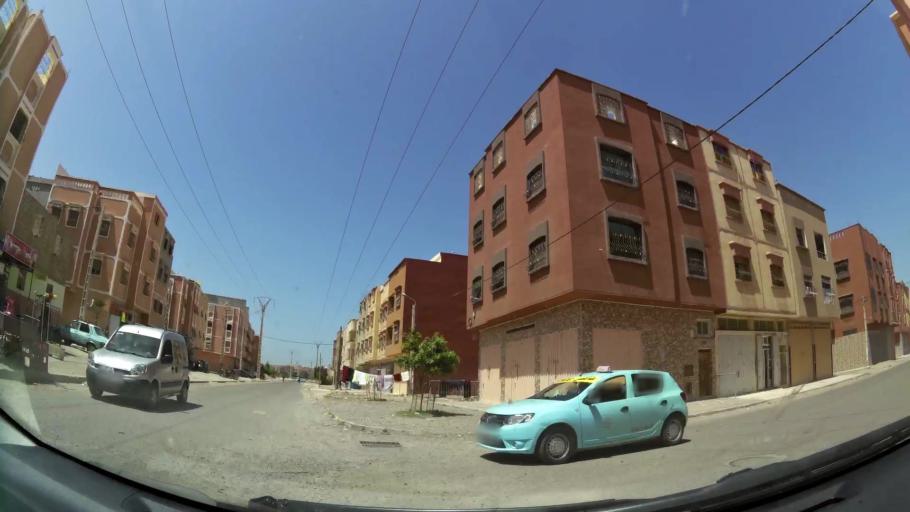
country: MA
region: Souss-Massa-Draa
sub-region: Inezgane-Ait Mellou
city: Inezgane
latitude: 30.3317
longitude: -9.4985
